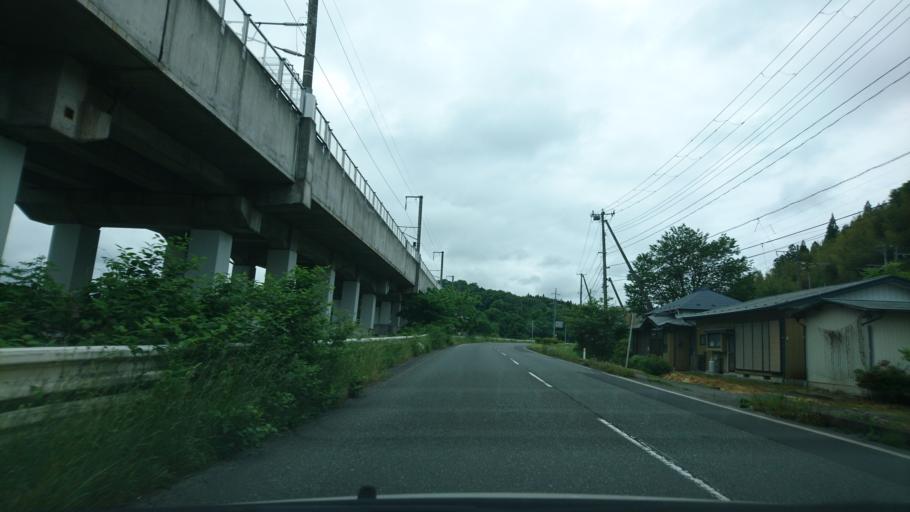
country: JP
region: Iwate
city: Ichinoseki
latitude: 38.8998
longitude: 141.1291
